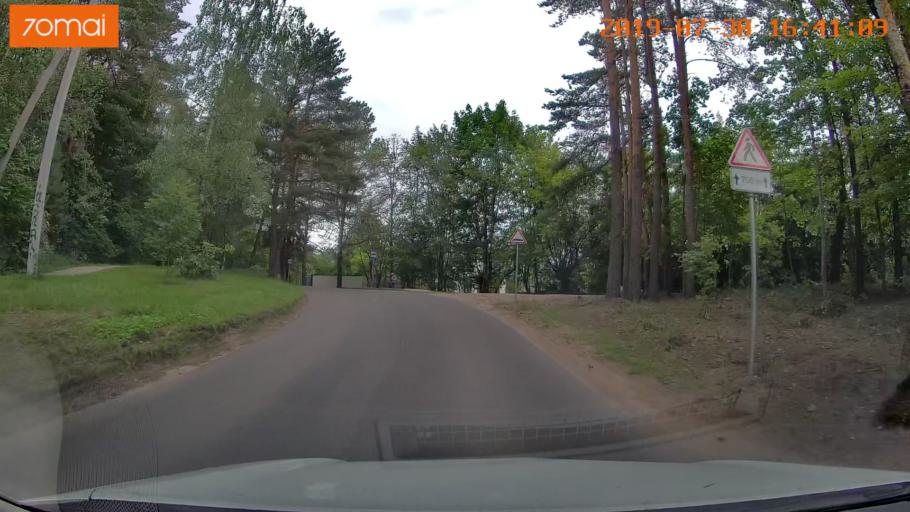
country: LT
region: Vilnius County
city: Rasos
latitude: 54.7095
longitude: 25.3578
